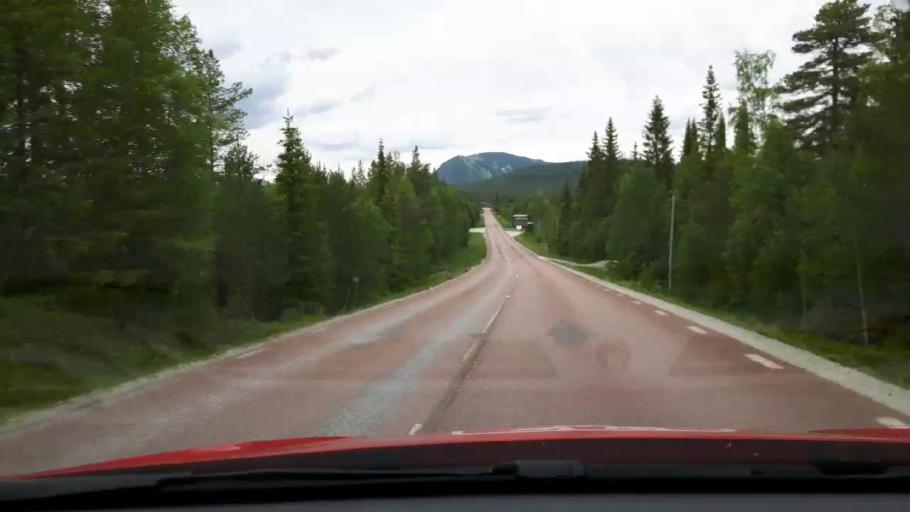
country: NO
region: Hedmark
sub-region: Engerdal
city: Engerdal
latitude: 62.5144
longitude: 12.6038
